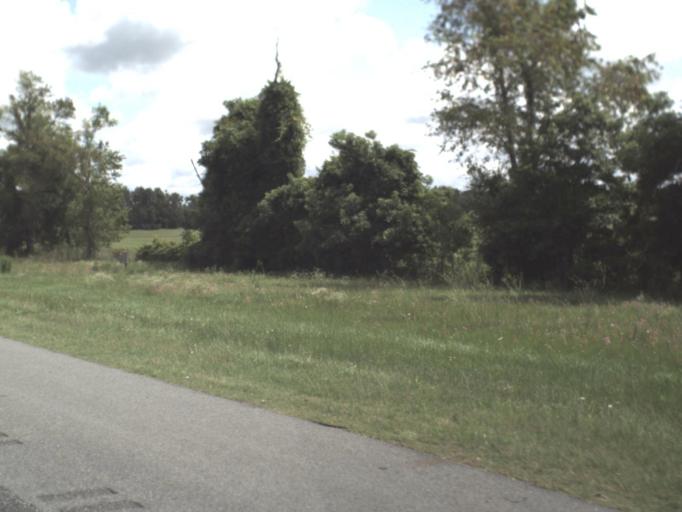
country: US
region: Florida
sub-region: Alachua County
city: High Springs
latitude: 30.0066
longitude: -82.6041
